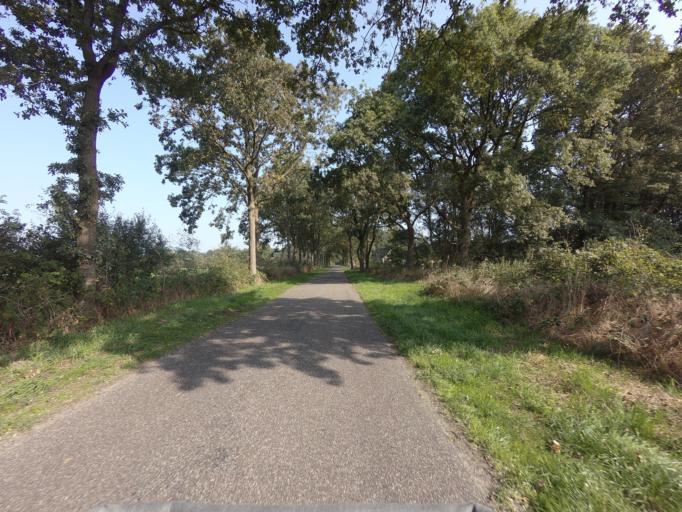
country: NL
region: Drenthe
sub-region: Gemeente Tynaarlo
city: Vries
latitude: 53.1334
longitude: 6.5285
